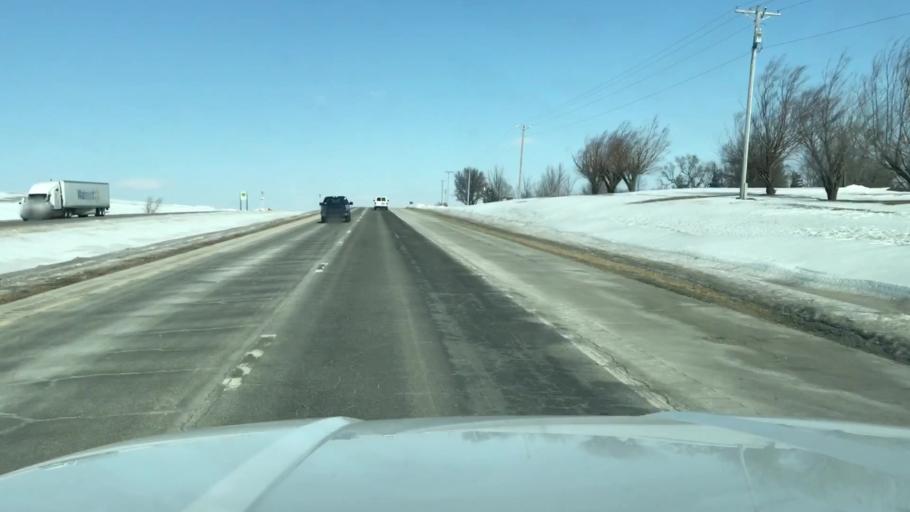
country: US
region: Missouri
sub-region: Nodaway County
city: Maryville
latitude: 40.2967
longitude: -94.8750
